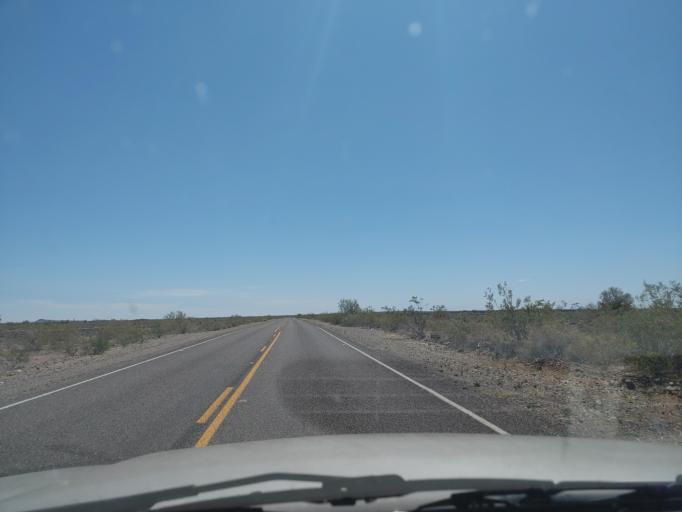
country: US
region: Arizona
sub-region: Maricopa County
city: Gila Bend
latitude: 32.9252
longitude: -113.2915
